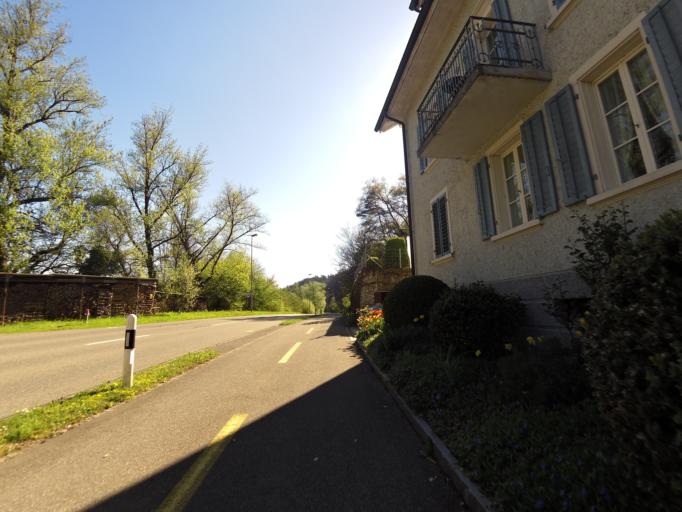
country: CH
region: Aargau
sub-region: Bezirk Zurzach
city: Koblenz
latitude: 47.5983
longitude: 8.2184
